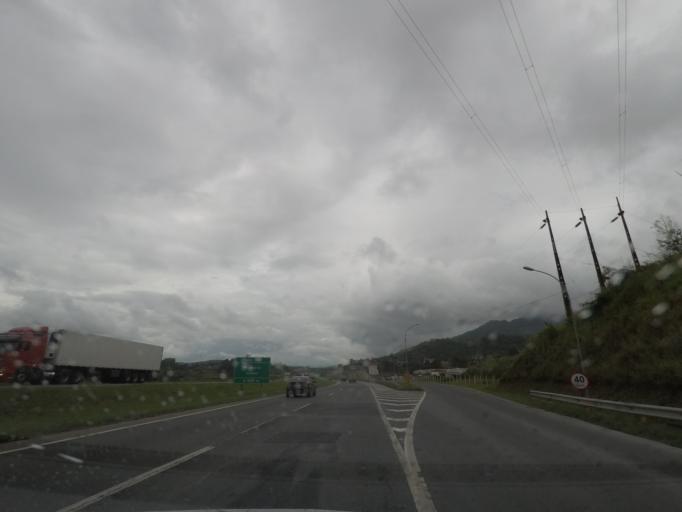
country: BR
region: Sao Paulo
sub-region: Miracatu
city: Miracatu
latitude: -24.2920
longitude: -47.4694
